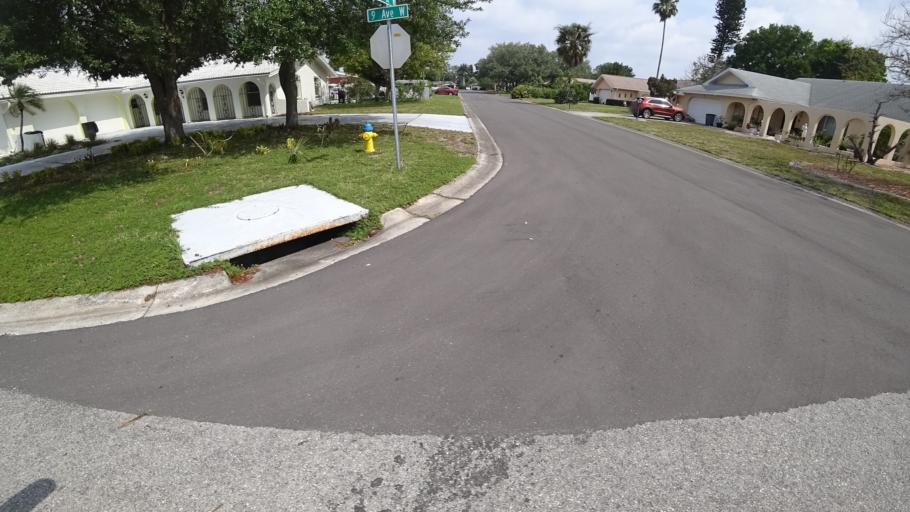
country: US
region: Florida
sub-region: Manatee County
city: West Bradenton
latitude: 27.4913
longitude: -82.6226
